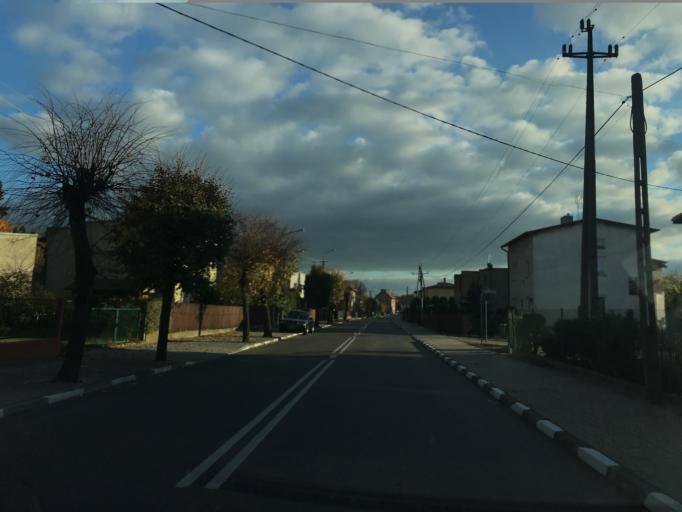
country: PL
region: Warmian-Masurian Voivodeship
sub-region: Powiat dzialdowski
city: Lidzbark
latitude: 53.2661
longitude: 19.8243
